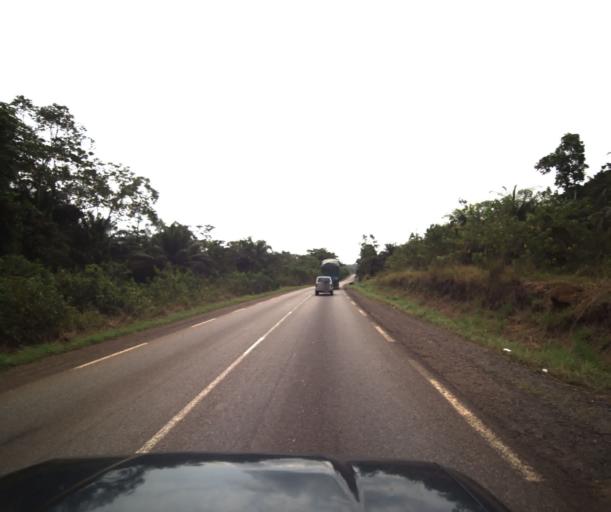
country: CM
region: Littoral
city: Edea
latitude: 3.8371
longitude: 10.4231
